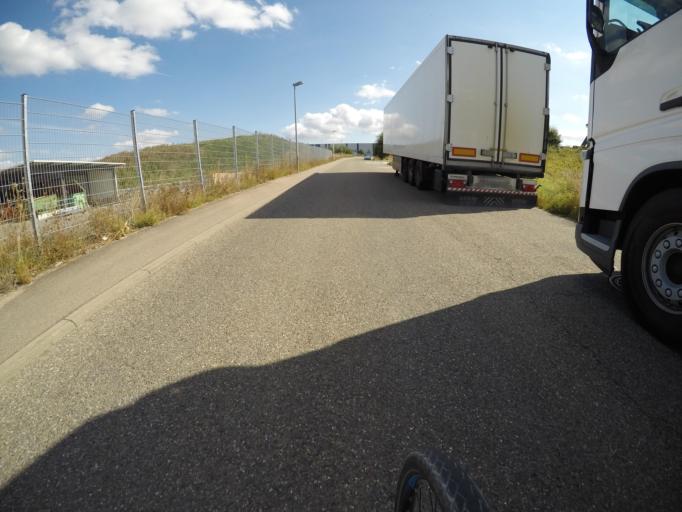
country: DE
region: Baden-Wuerttemberg
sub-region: Regierungsbezirk Stuttgart
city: Herbrechtingen
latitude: 48.6168
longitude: 10.2060
